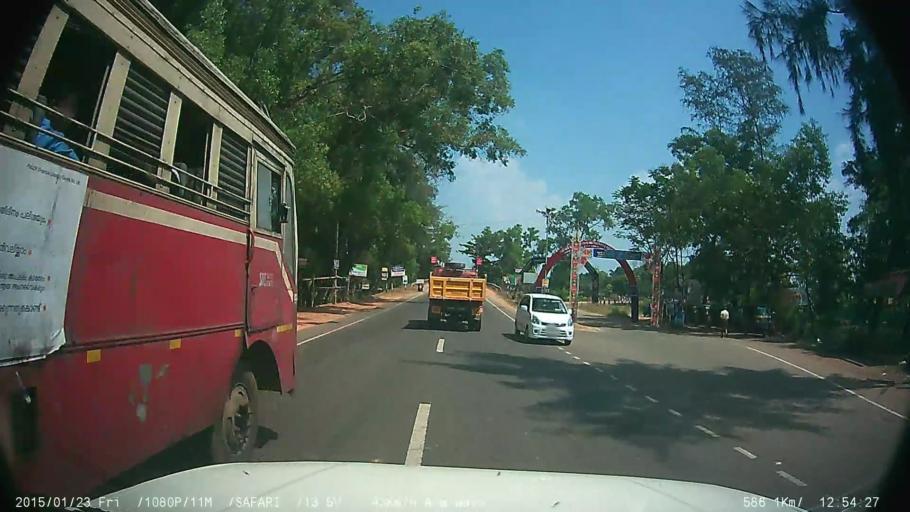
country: IN
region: Kerala
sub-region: Kottayam
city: Changanacheri
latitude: 9.4187
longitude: 76.4901
